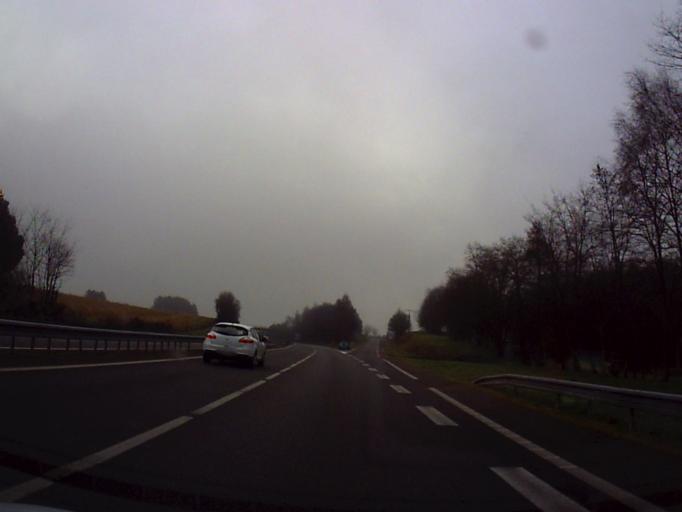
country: FR
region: Brittany
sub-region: Departement du Morbihan
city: Guillac
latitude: 47.8729
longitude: -2.4186
